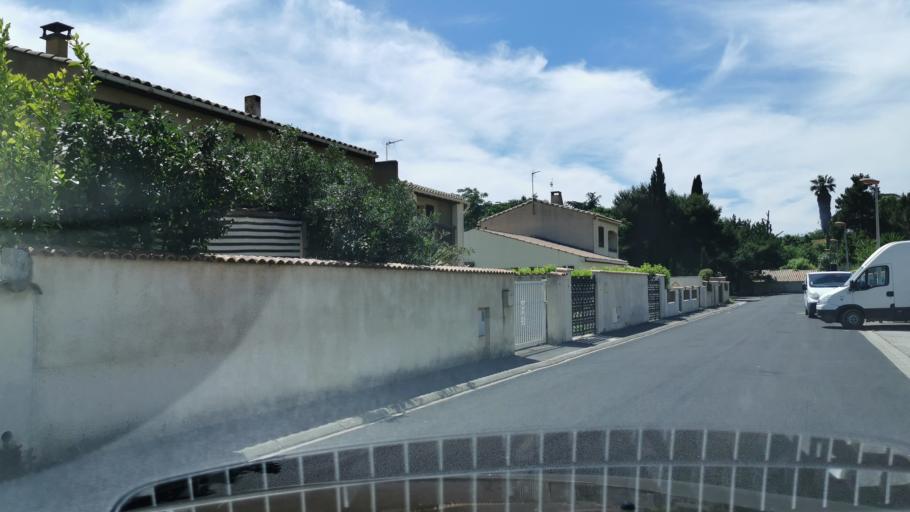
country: FR
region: Languedoc-Roussillon
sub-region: Departement de l'Aude
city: Narbonne
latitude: 43.1866
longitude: 2.9822
